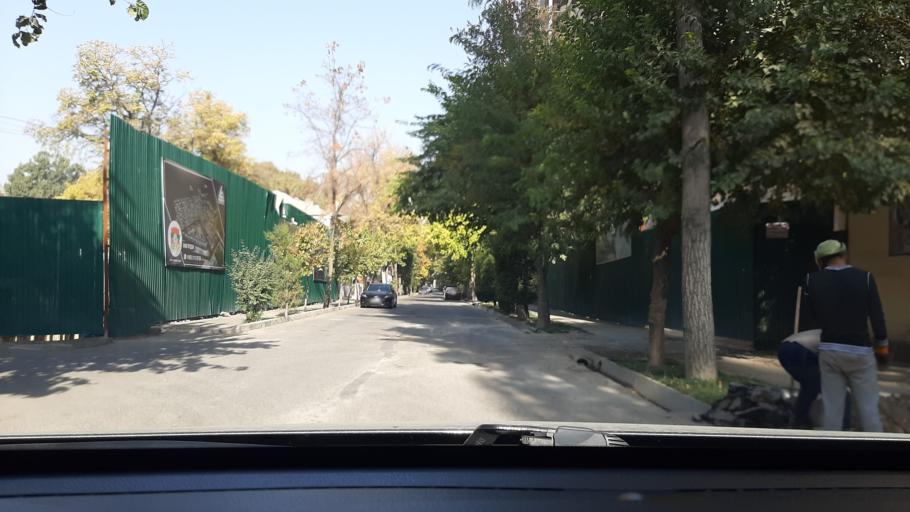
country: TJ
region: Dushanbe
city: Dushanbe
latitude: 38.5648
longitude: 68.7933
